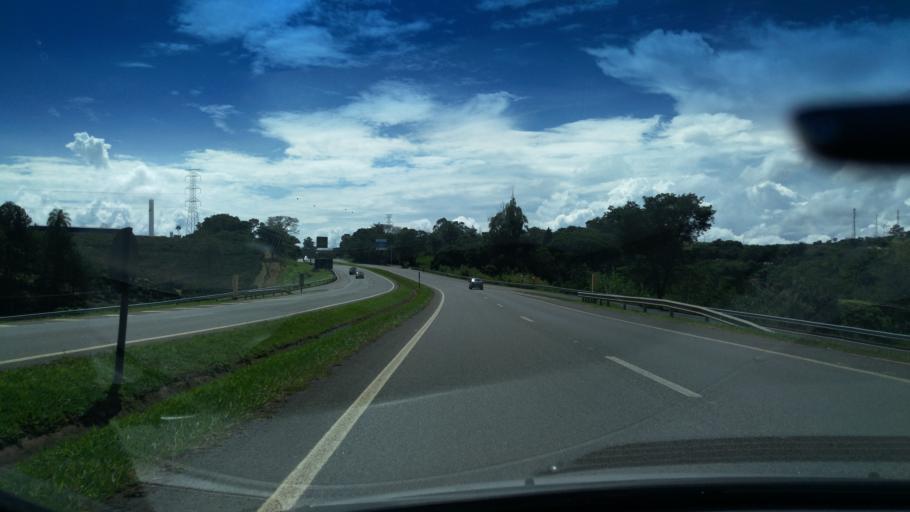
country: BR
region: Sao Paulo
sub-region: Santo Antonio Do Jardim
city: Espirito Santo do Pinhal
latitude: -22.1907
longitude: -46.7684
